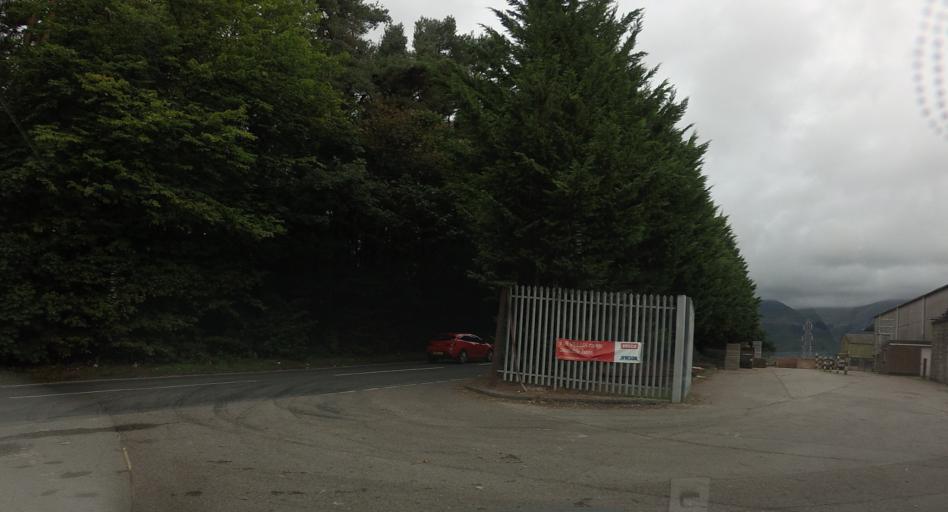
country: GB
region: Scotland
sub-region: Clackmannanshire
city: Alloa
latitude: 56.1332
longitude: -3.7947
